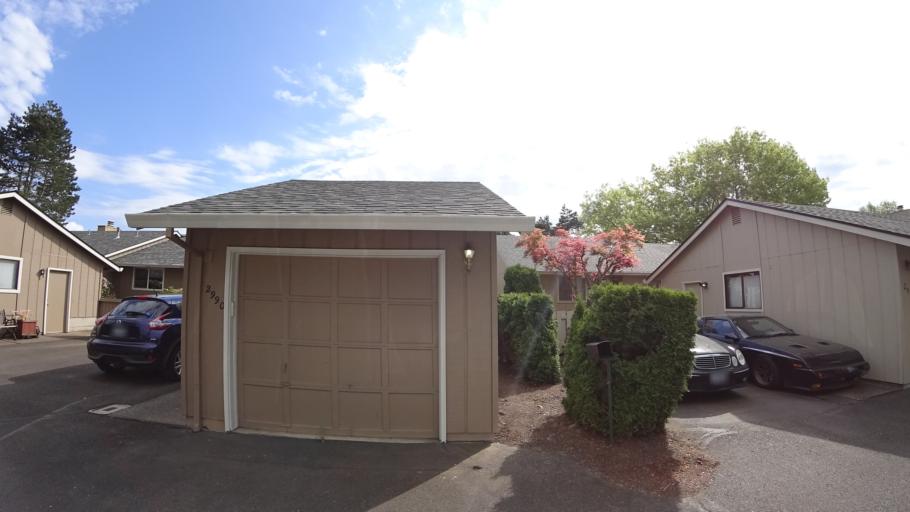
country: US
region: Oregon
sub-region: Washington County
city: Hillsboro
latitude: 45.4971
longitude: -122.9591
